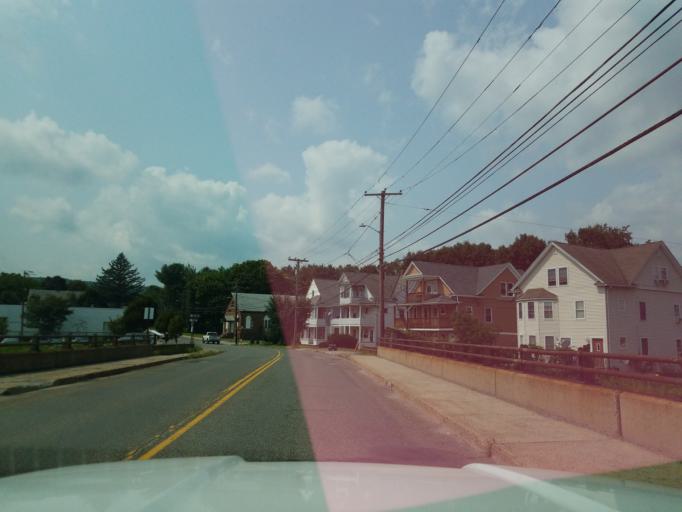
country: US
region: Connecticut
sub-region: Litchfield County
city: Torrington
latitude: 41.7958
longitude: -73.1173
